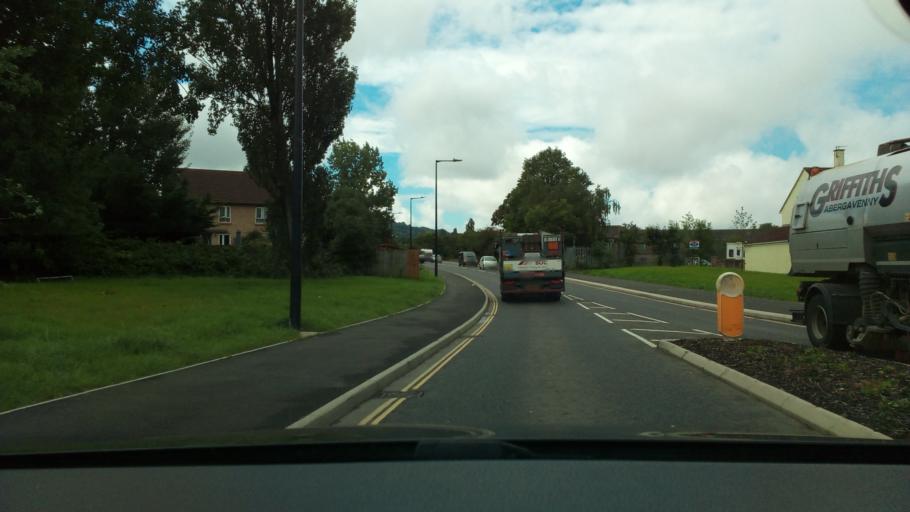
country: GB
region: England
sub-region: North Somerset
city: Dundry
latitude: 51.4119
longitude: -2.6150
